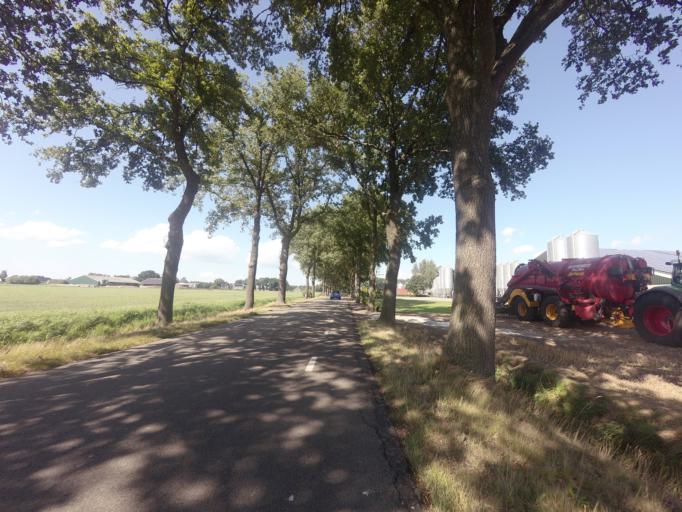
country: NL
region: Overijssel
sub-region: Gemeente Twenterand
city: Den Ham
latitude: 52.5592
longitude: 6.4343
